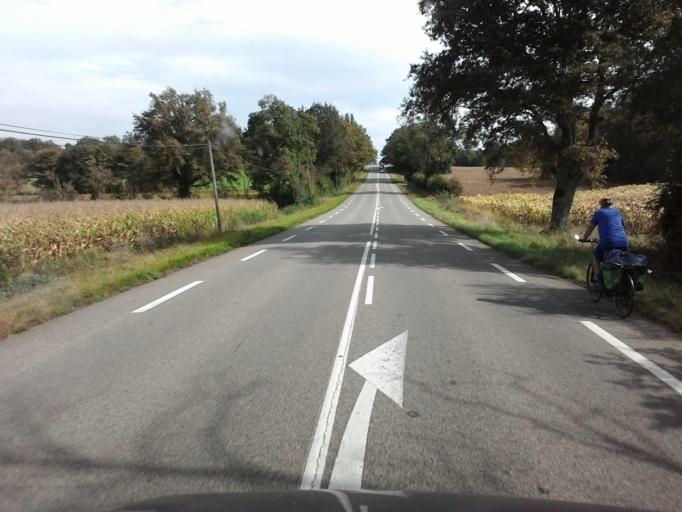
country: FR
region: Rhone-Alpes
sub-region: Departement de l'Ain
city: Mezeriat
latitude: 46.2554
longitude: 5.0639
